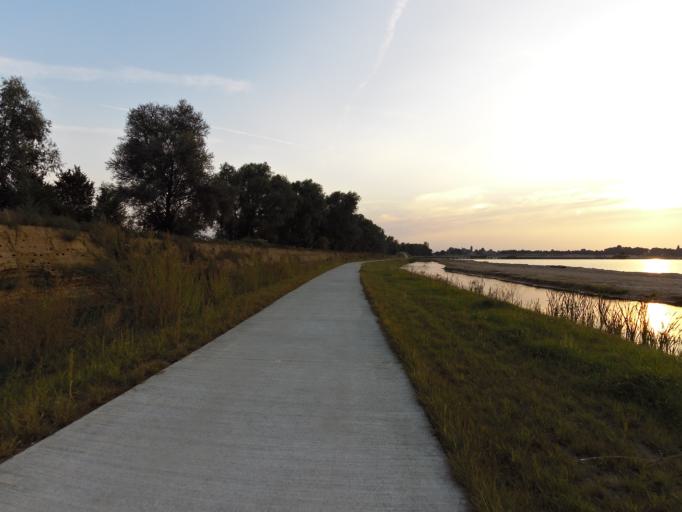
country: DE
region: North Rhine-Westphalia
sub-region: Regierungsbezirk Dusseldorf
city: Kleve
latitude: 51.8632
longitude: 6.1353
